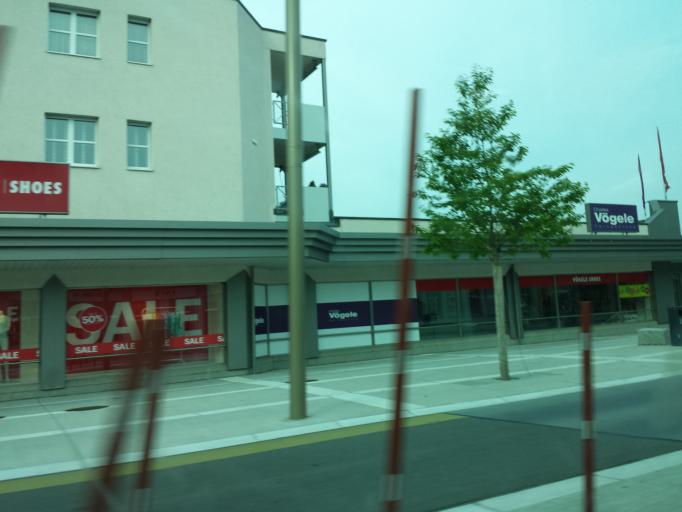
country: CH
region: Appenzell Innerrhoden
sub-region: Appenzell Inner Rhodes
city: Balgach
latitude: 47.4074
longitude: 9.6306
